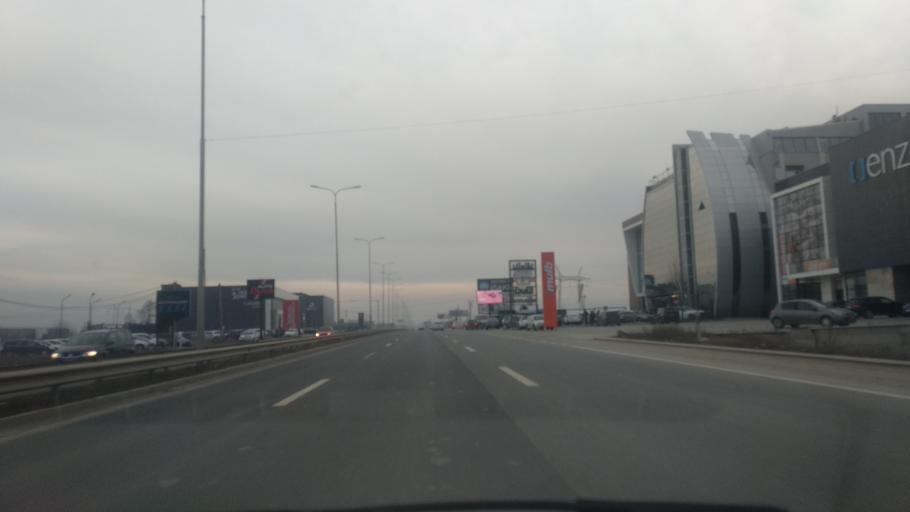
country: XK
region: Pristina
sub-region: Kosovo Polje
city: Kosovo Polje
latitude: 42.5970
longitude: 21.1305
